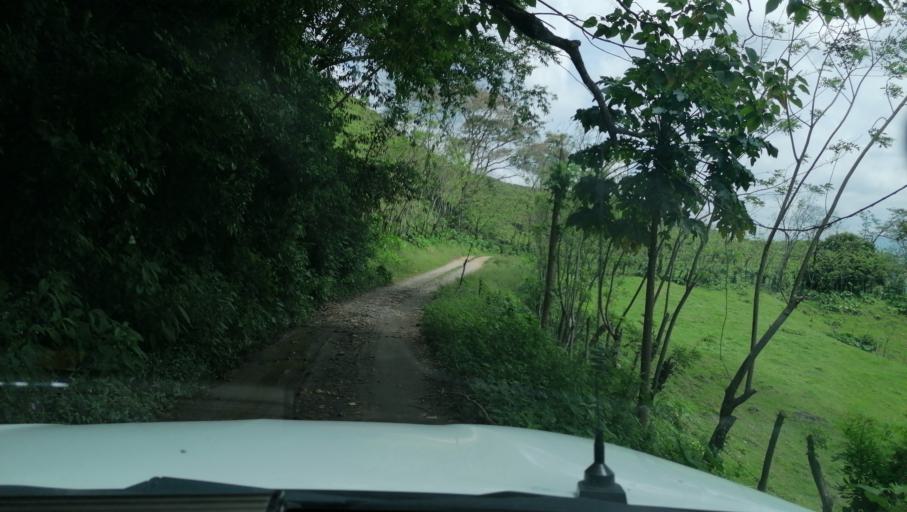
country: MX
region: Chiapas
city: Ixtacomitan
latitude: 17.4444
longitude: -93.2010
